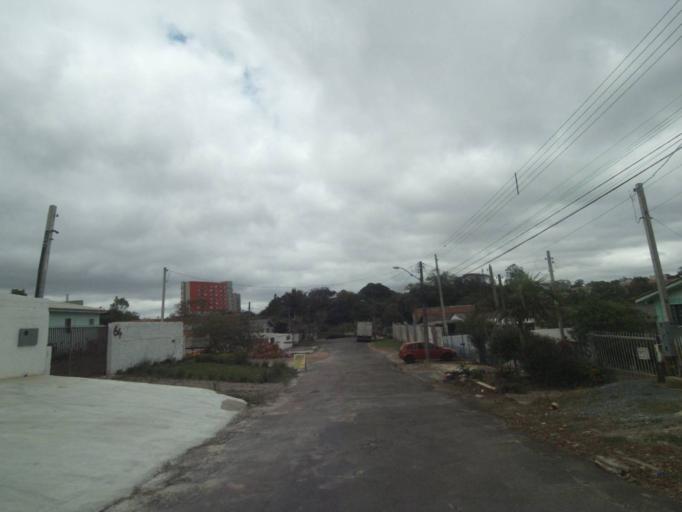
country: BR
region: Parana
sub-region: Pinhais
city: Pinhais
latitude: -25.4020
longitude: -49.2182
